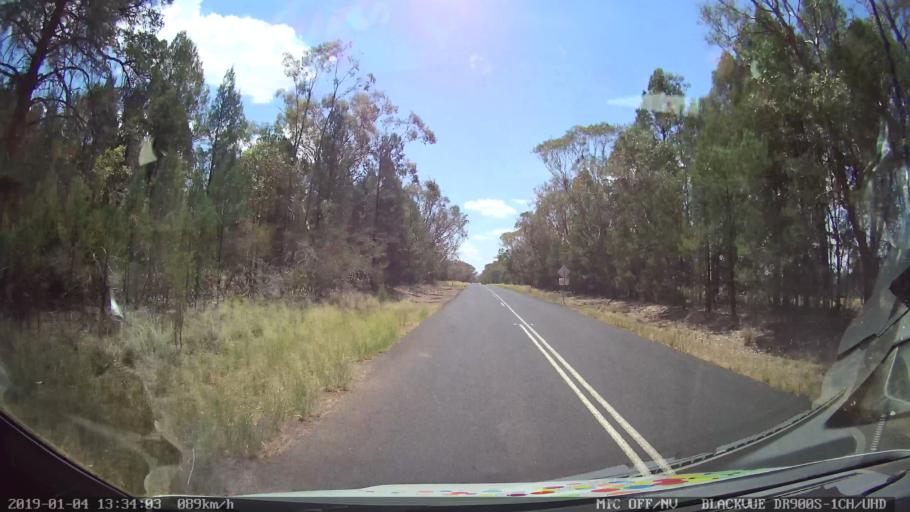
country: AU
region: New South Wales
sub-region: Dubbo Municipality
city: Dubbo
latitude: -32.5908
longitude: 148.5374
